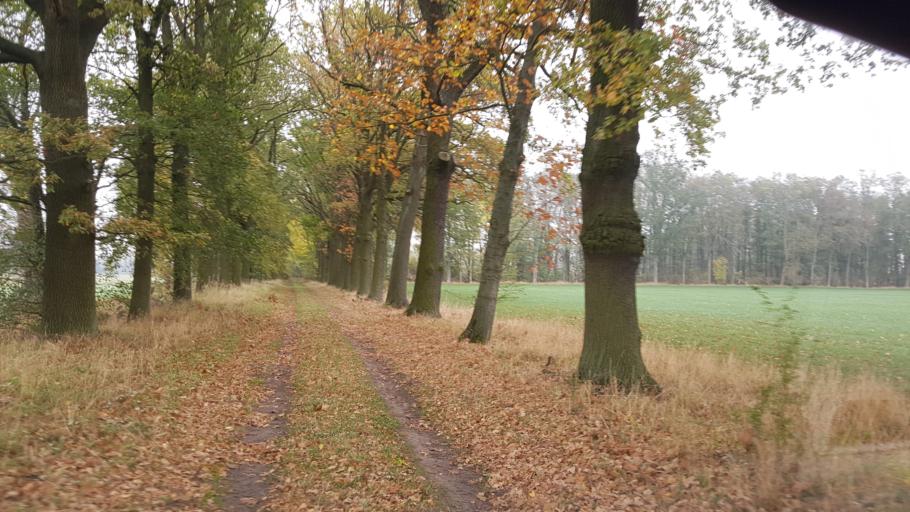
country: DE
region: Brandenburg
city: Schonewalde
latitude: 51.6955
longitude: 13.6034
